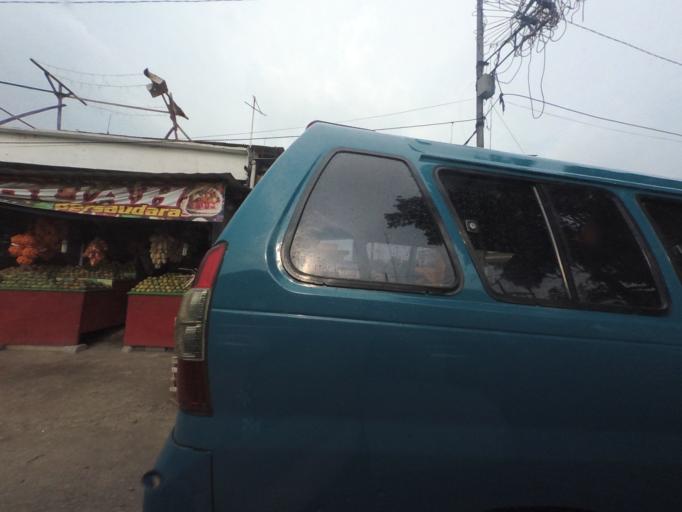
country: ID
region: West Java
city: Cicurug
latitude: -6.7589
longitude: 106.7994
